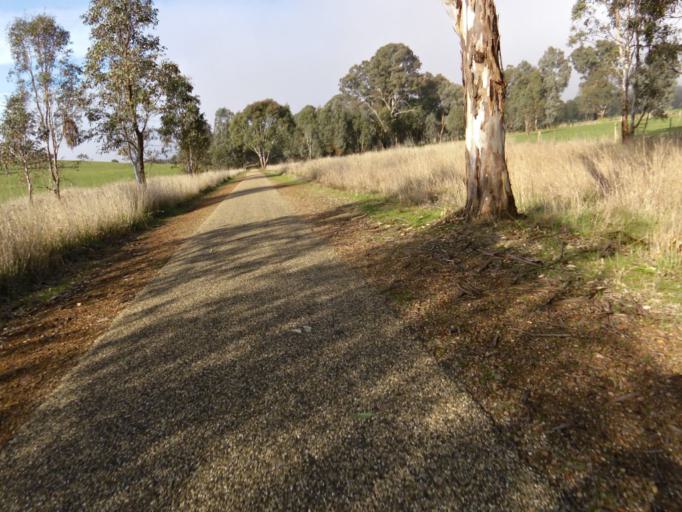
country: AU
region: Victoria
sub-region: Wangaratta
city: Wangaratta
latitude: -36.4450
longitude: 146.5512
